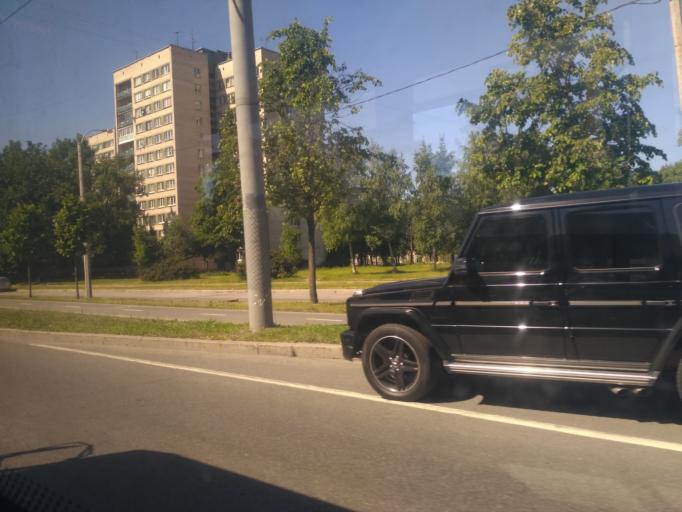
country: RU
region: Leningrad
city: Kalininskiy
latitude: 59.9727
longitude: 30.4130
